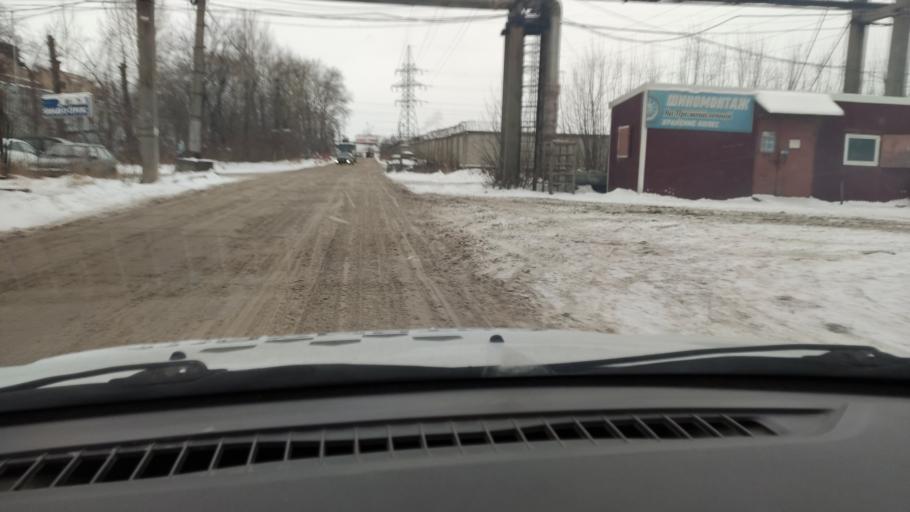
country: RU
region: Perm
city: Gamovo
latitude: 57.9208
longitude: 56.1509
